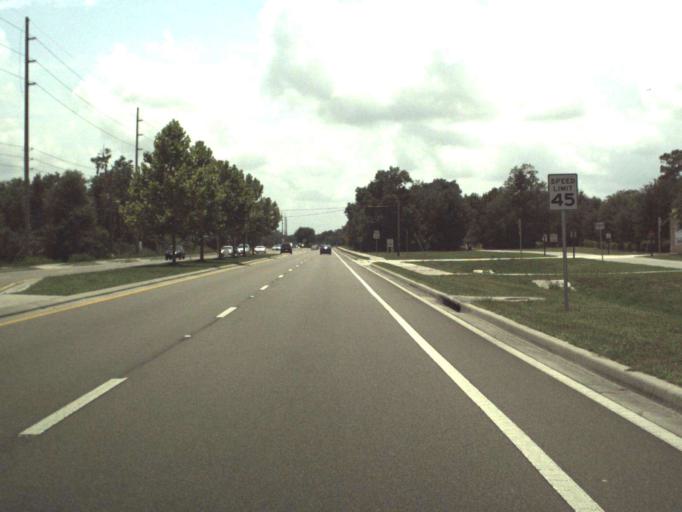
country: US
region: Florida
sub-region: Seminole County
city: Oviedo
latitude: 28.6328
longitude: -81.2390
